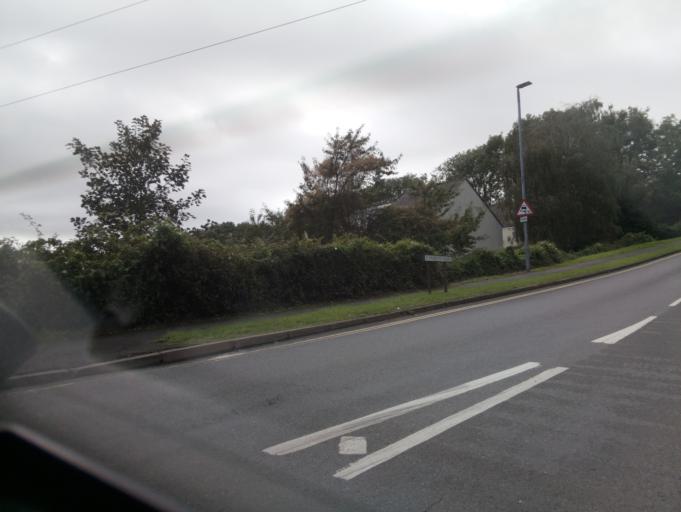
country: GB
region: England
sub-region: Devon
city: Kingsbridge
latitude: 50.2889
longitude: -3.7800
